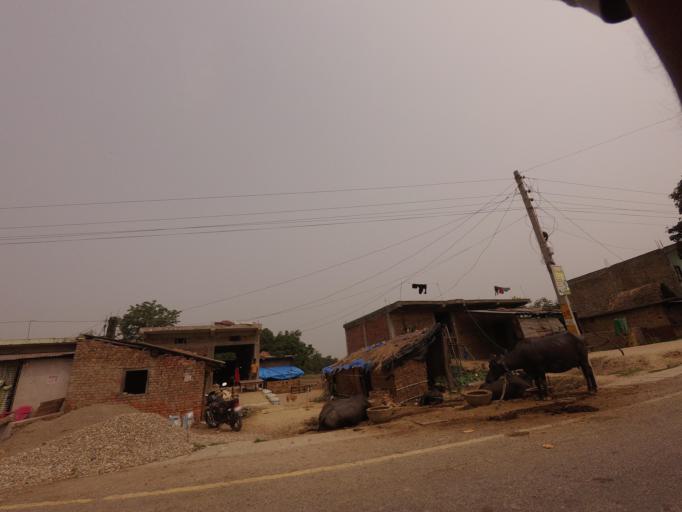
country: IN
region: Uttar Pradesh
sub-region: Maharajganj
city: Nautanwa
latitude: 27.4957
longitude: 83.3276
